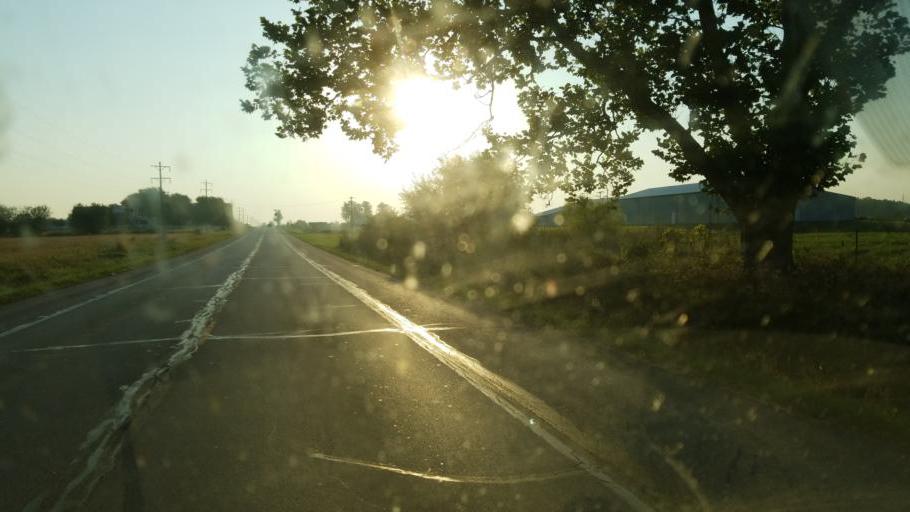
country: US
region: Indiana
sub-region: LaGrange County
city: Lagrange
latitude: 41.6408
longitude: -85.4997
